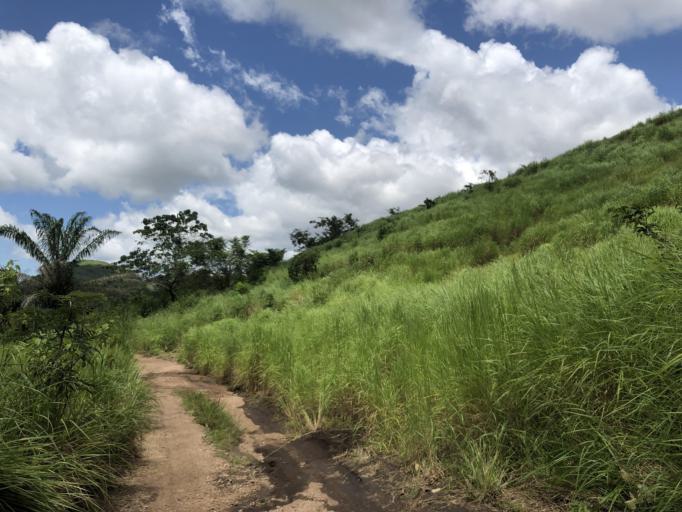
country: SL
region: Northern Province
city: Makeni
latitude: 8.8538
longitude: -12.0623
